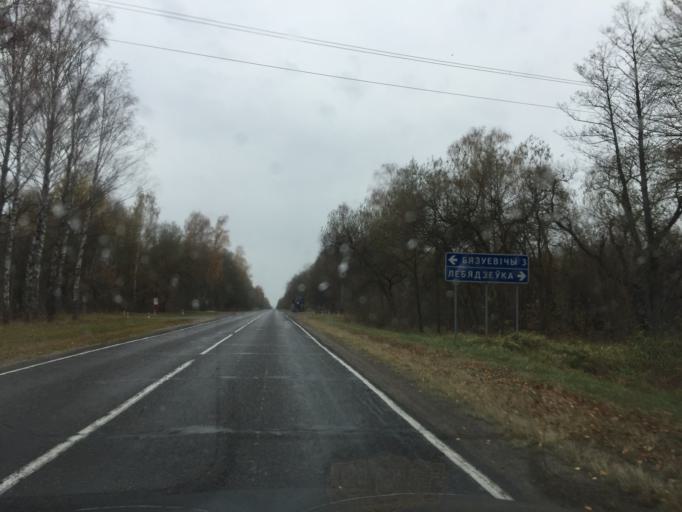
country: BY
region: Mogilev
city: Slawharad
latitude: 53.3674
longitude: 30.8556
